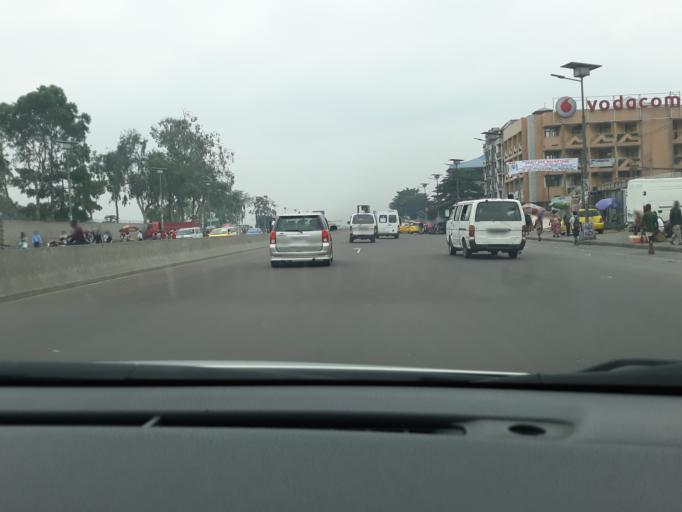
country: CD
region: Kinshasa
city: Masina
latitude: -4.3901
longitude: 15.3740
